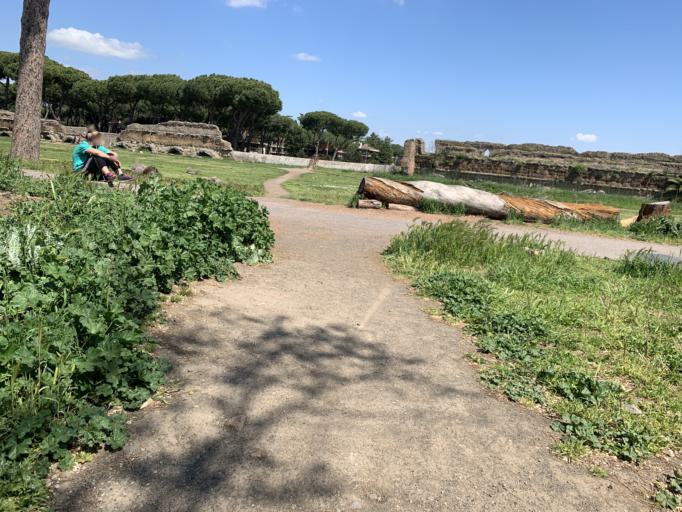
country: IT
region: Latium
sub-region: Citta metropolitana di Roma Capitale
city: Ciampino
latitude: 41.8463
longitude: 12.5627
